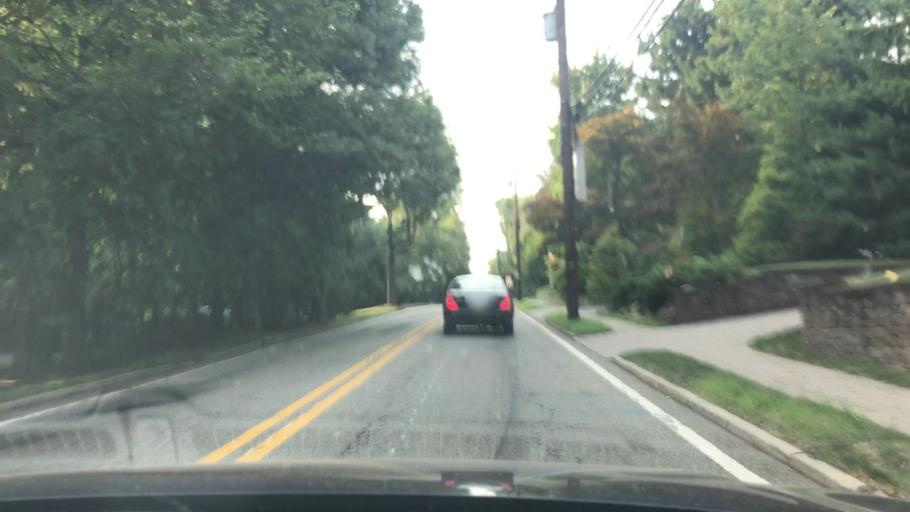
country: US
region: New Jersey
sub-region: Bergen County
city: Norwood
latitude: 40.9866
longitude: -73.9613
